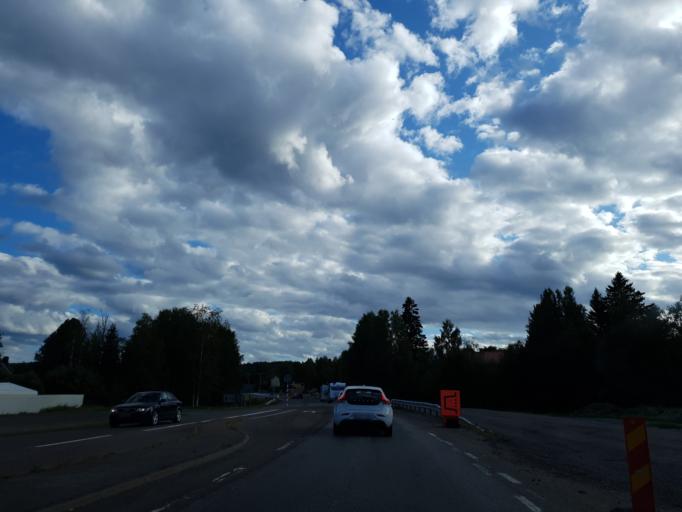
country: SE
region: Vaesternorrland
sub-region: Haernoesands Kommun
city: Haernoesand
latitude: 62.6734
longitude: 17.8400
